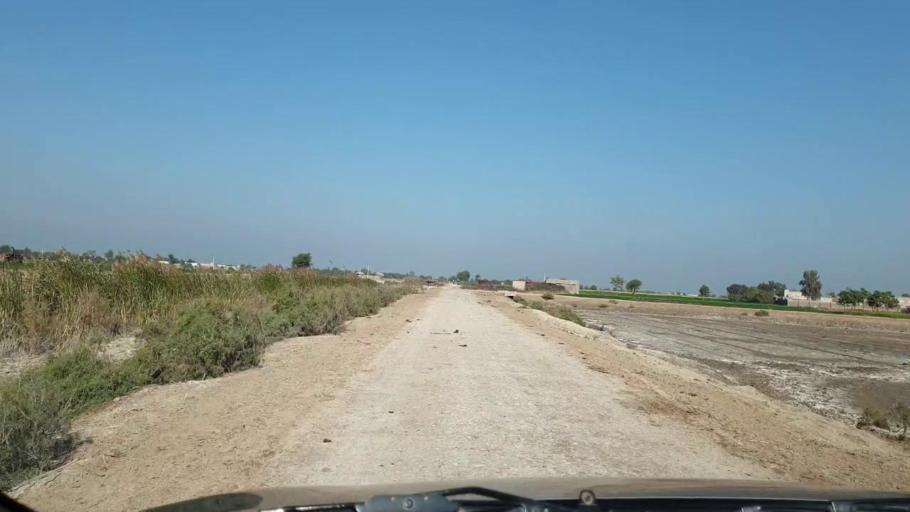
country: PK
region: Sindh
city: Sinjhoro
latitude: 25.9421
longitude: 68.7527
